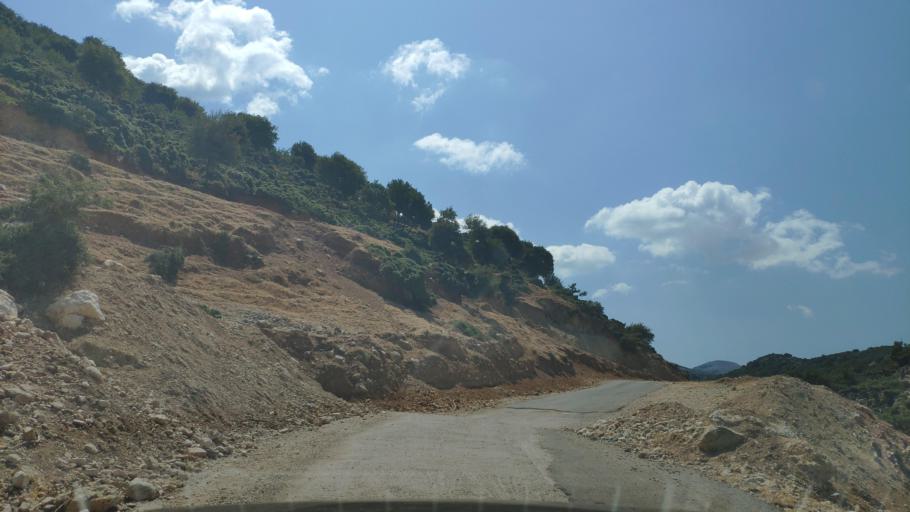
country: GR
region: West Greece
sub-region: Nomos Aitolias kai Akarnanias
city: Monastirakion
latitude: 38.8108
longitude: 20.9404
